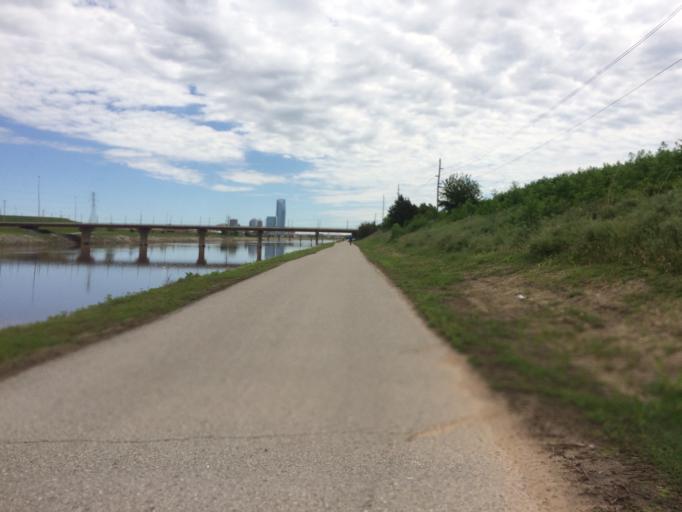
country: US
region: Oklahoma
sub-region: Oklahoma County
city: Oklahoma City
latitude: 35.4581
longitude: -97.5583
